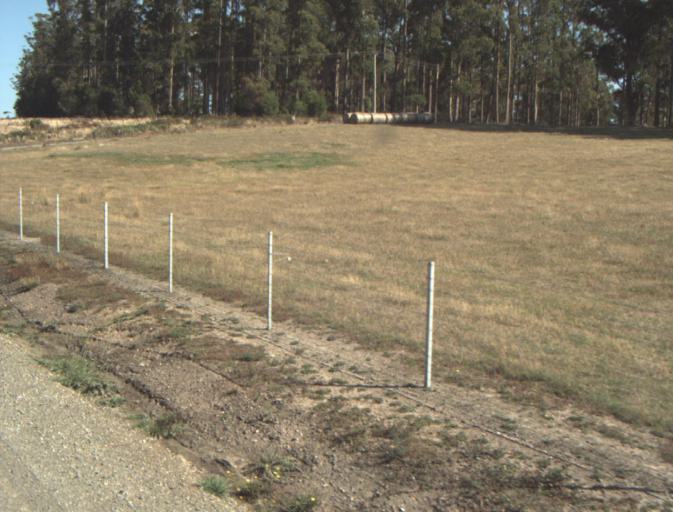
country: AU
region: Tasmania
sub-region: Launceston
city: Mayfield
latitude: -41.2300
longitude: 147.2357
